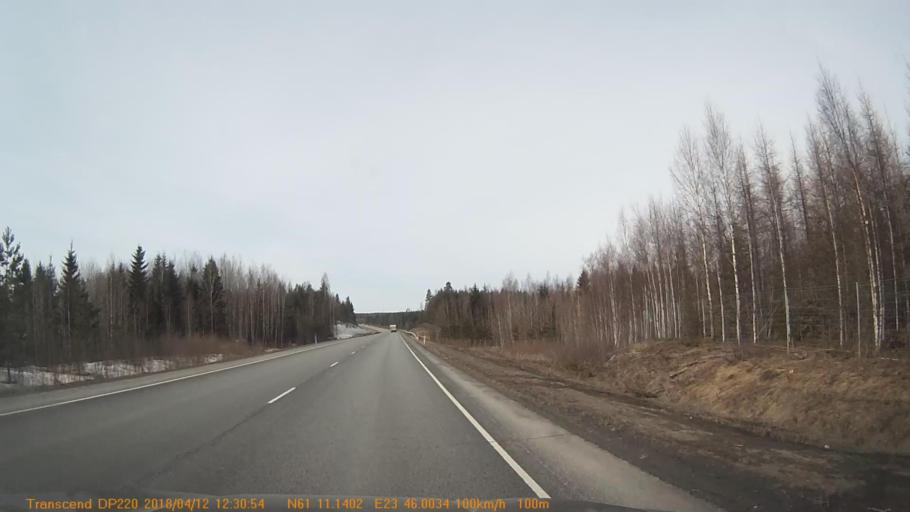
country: FI
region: Pirkanmaa
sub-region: Etelae-Pirkanmaa
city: Viiala
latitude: 61.1858
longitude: 23.7658
